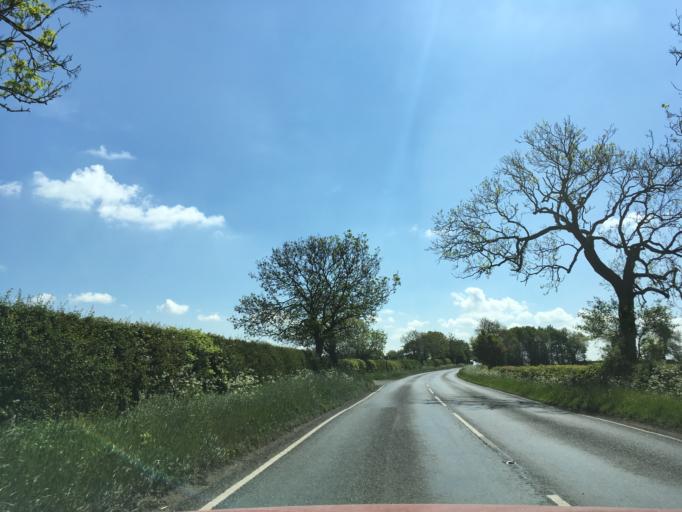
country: GB
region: England
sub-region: Northamptonshire
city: Brackley
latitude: 52.0244
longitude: -1.1136
